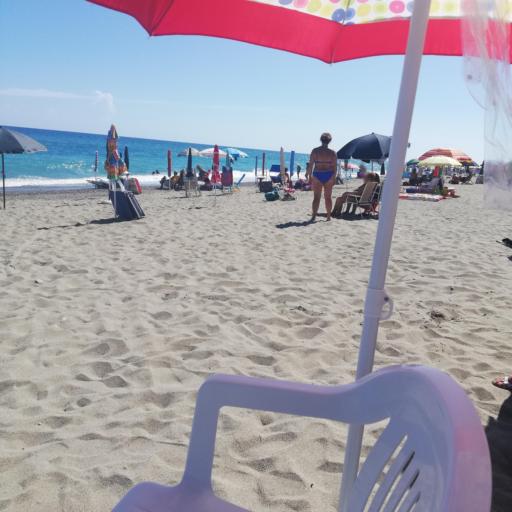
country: IT
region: Calabria
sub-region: Provincia di Cosenza
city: Caloppezzati
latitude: 39.5479
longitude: 16.8533
